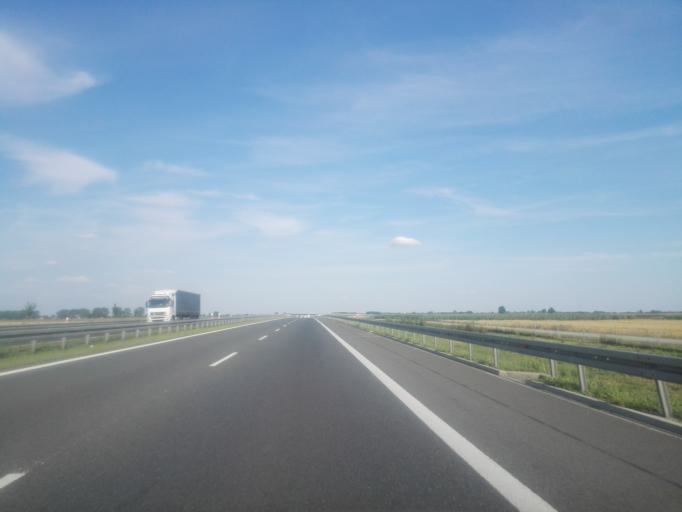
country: PL
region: Lower Silesian Voivodeship
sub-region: Powiat olesnicki
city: Dobroszyce
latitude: 51.2257
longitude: 17.2809
